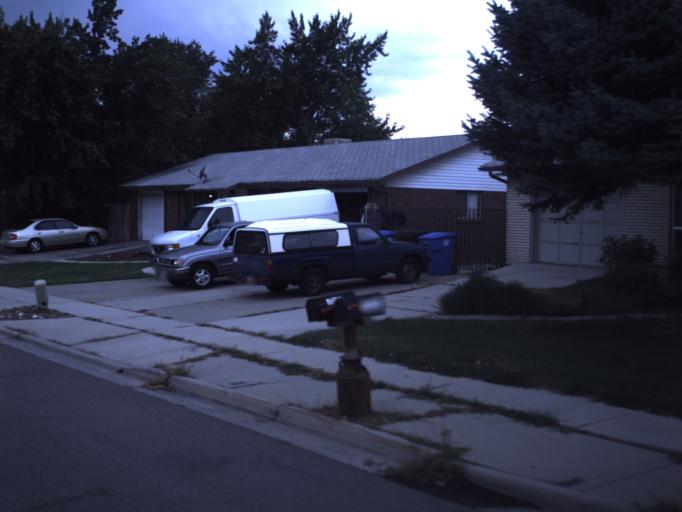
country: US
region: Utah
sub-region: Salt Lake County
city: Sandy City
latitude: 40.6145
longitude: -111.8693
